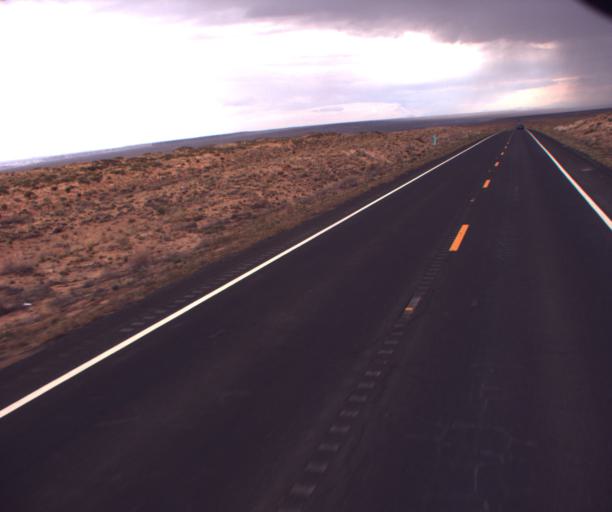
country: US
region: Arizona
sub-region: Coconino County
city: Tuba City
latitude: 36.2244
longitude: -111.0375
